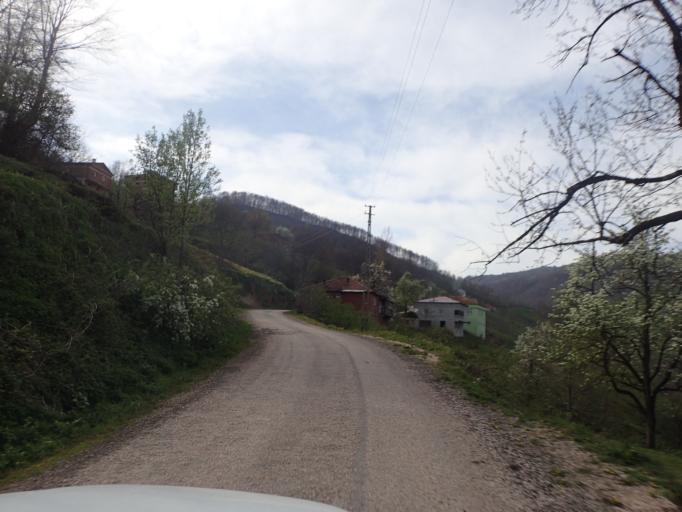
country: TR
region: Ordu
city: Aybasti
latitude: 40.7079
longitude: 37.2804
